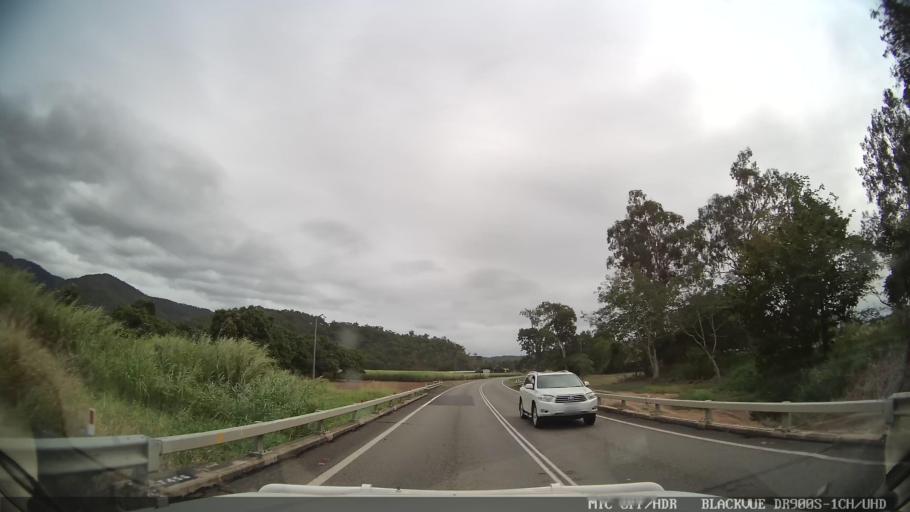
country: AU
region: Queensland
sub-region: Hinchinbrook
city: Ingham
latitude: -18.8621
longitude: 146.1696
